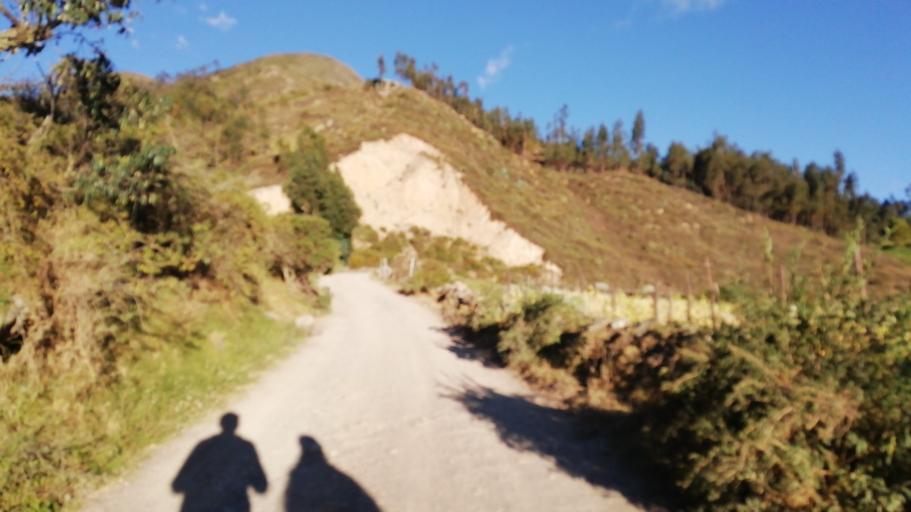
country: CO
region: Boyaca
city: Gameza
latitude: 5.7842
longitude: -72.7990
